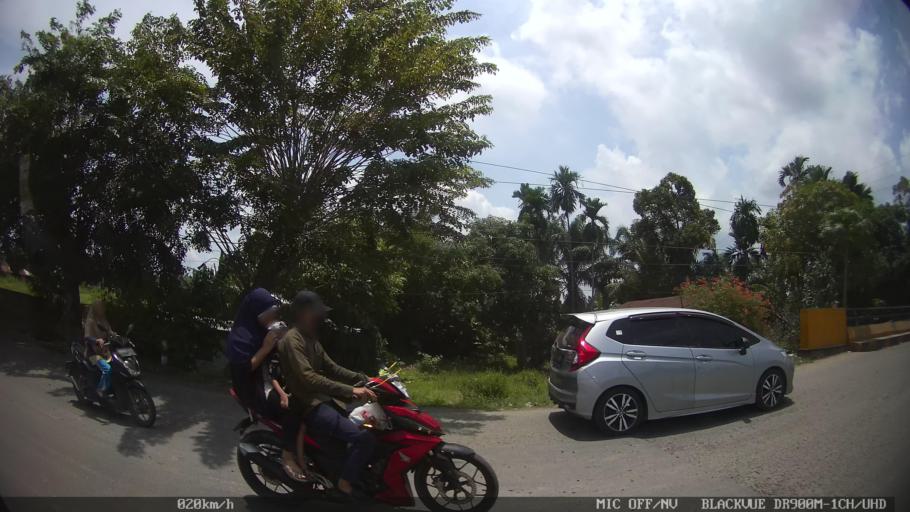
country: ID
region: North Sumatra
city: Labuhan Deli
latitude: 3.7192
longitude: 98.6675
